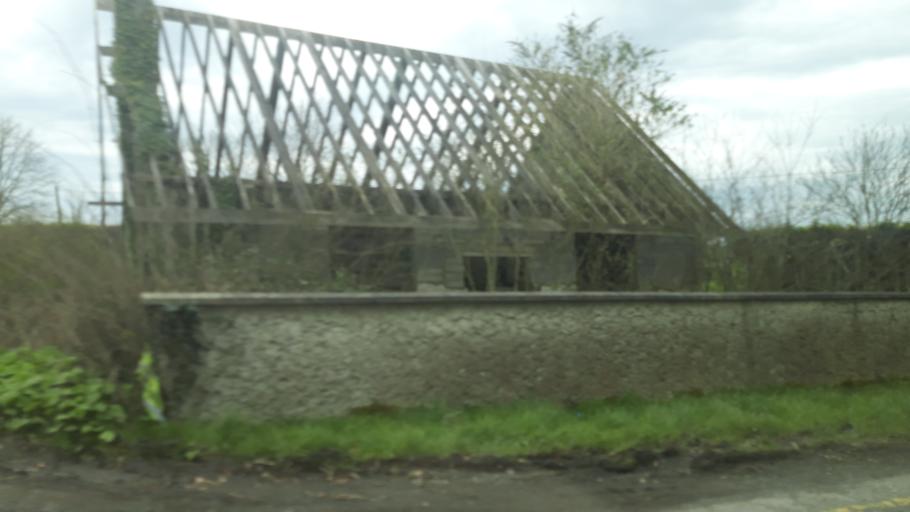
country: IE
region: Leinster
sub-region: Kildare
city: Prosperous
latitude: 53.2981
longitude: -6.7388
